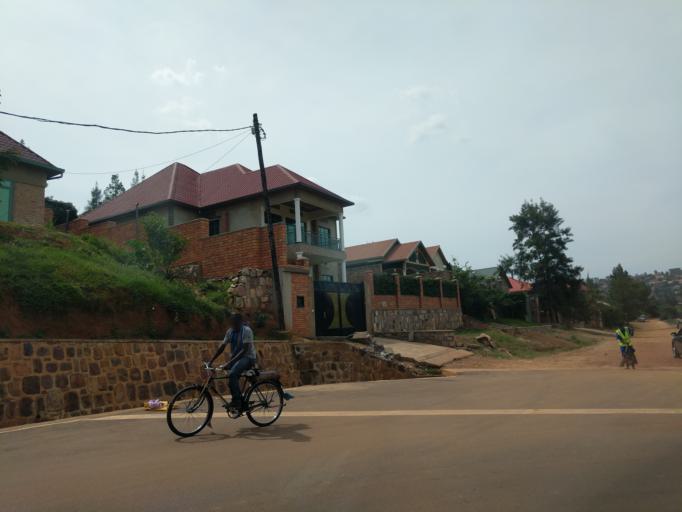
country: RW
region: Kigali
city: Kigali
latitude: -1.9747
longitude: 30.1188
